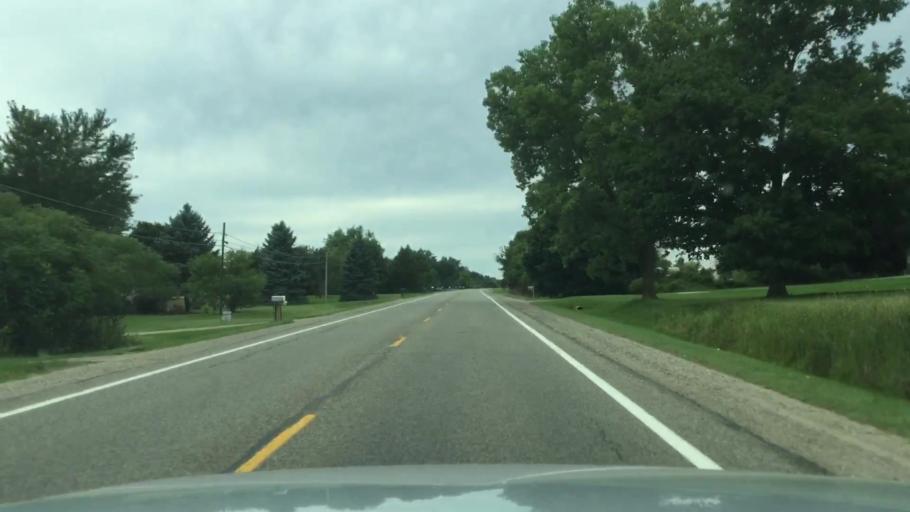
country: US
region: Michigan
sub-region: Shiawassee County
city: Durand
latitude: 42.9346
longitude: -84.0129
